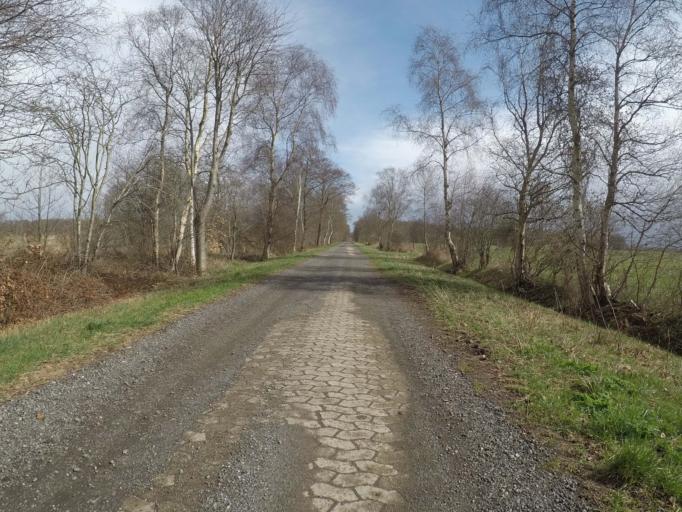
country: DE
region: Lower Saxony
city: Elmlohe
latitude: 53.6035
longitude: 8.6982
